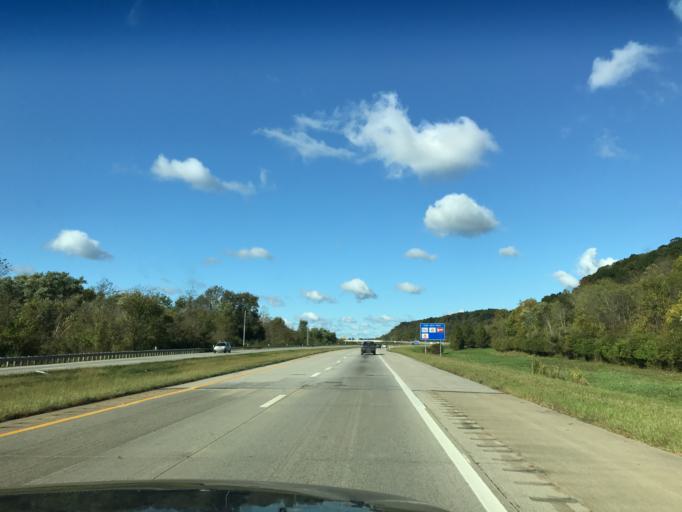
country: US
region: Ohio
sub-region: Athens County
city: Athens
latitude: 39.3343
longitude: -82.0215
